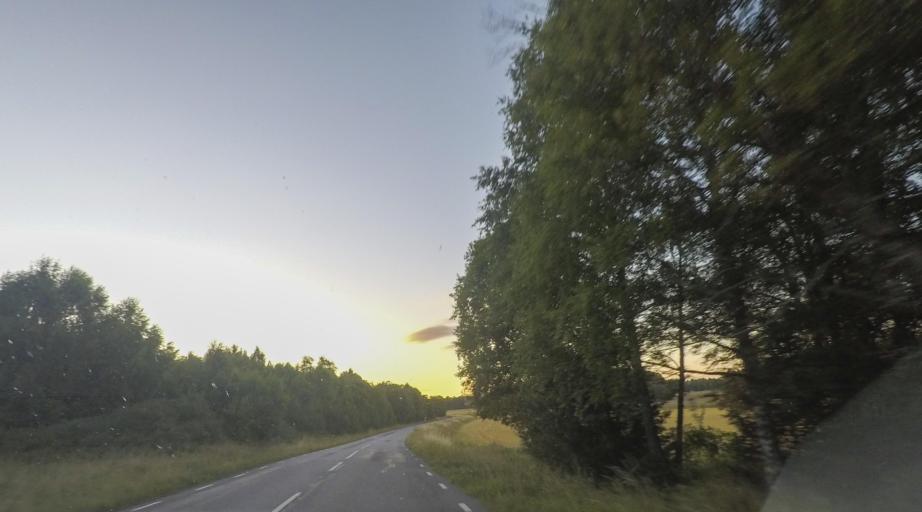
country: SE
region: Soedermanland
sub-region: Trosa Kommun
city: Trosa
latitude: 58.9810
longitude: 17.6877
